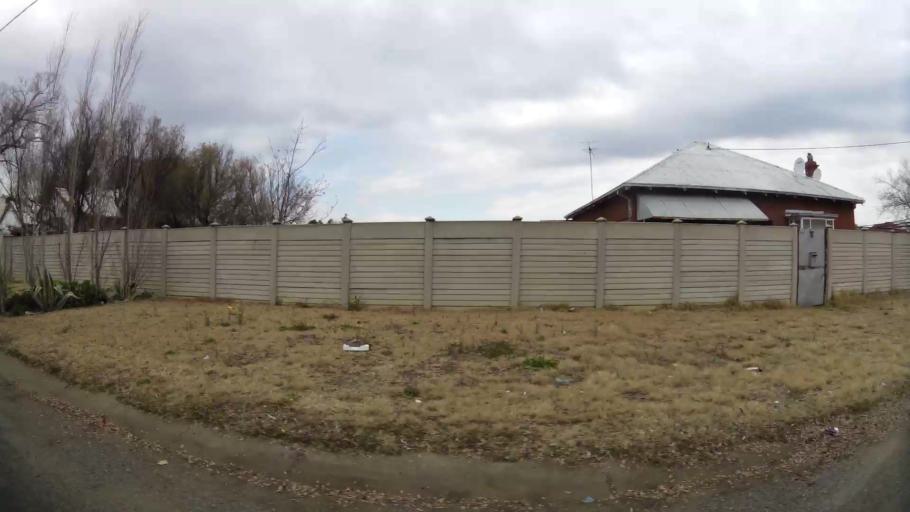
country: ZA
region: Orange Free State
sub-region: Fezile Dabi District Municipality
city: Kroonstad
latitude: -27.6561
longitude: 27.2411
